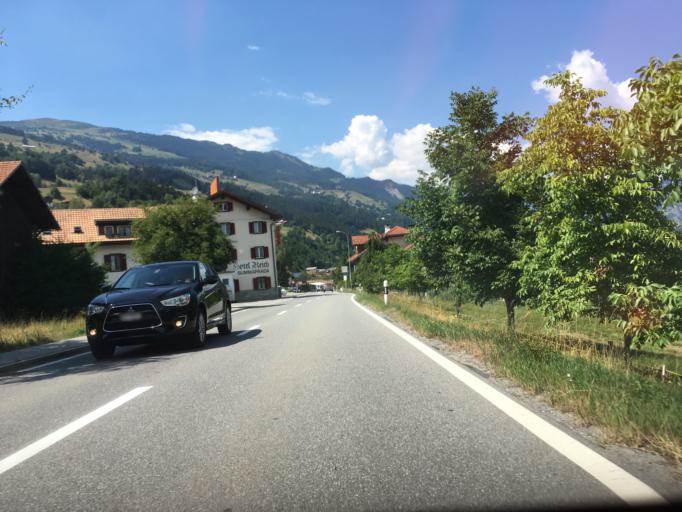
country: CH
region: Grisons
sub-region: Hinterrhein District
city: Cazis
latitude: 46.7130
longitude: 9.4347
